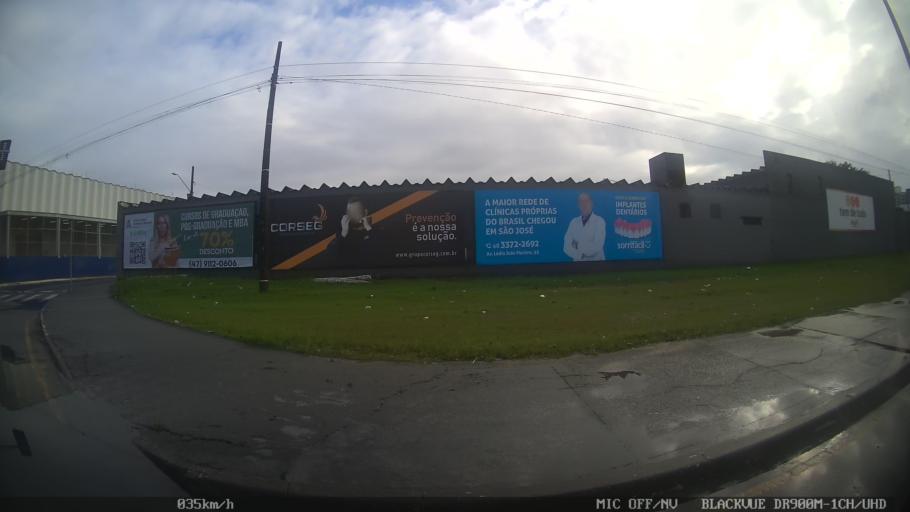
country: BR
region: Santa Catarina
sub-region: Sao Jose
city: Campinas
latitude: -27.6024
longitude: -48.6147
